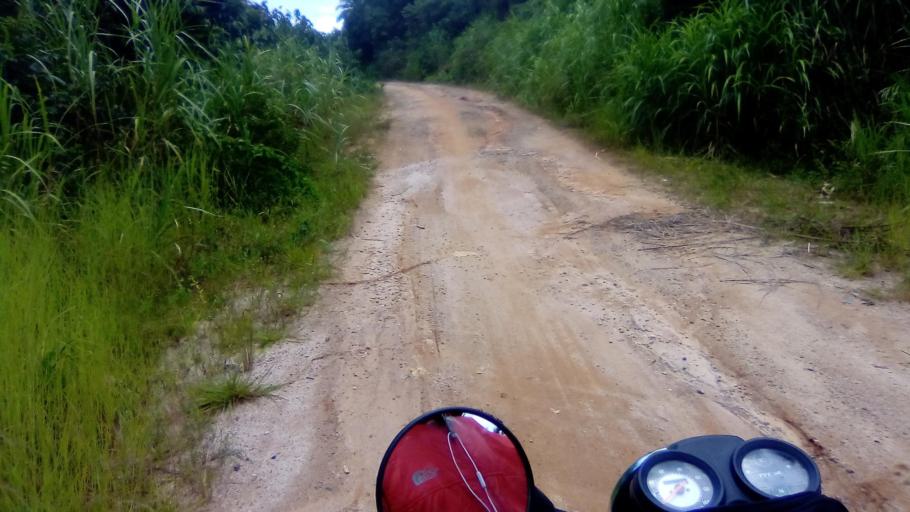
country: SL
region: Eastern Province
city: Simbakoro
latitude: 8.5478
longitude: -10.9293
